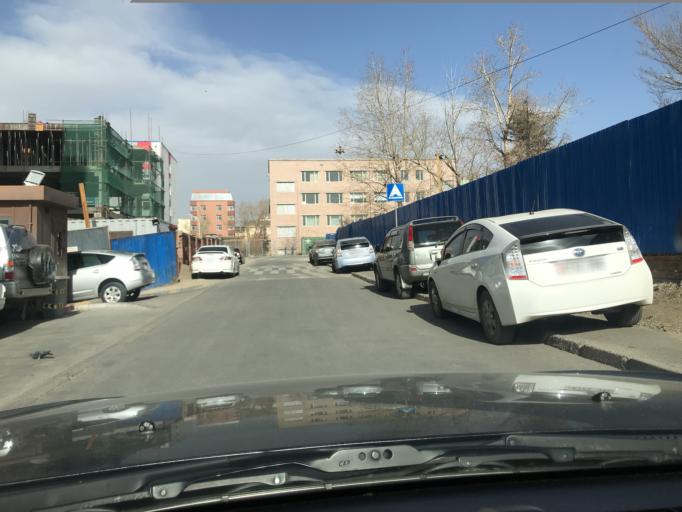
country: MN
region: Ulaanbaatar
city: Ulaanbaatar
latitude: 47.9211
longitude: 106.9399
